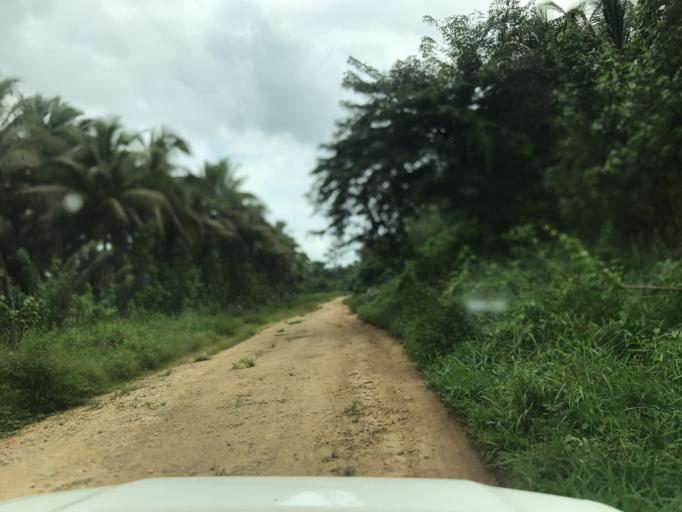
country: VU
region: Sanma
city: Port-Olry
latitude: -15.1868
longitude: 167.0213
